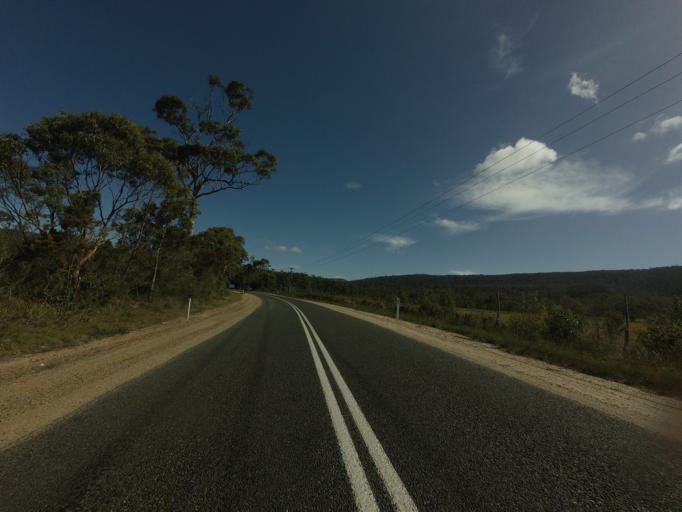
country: AU
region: Tasmania
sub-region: Break O'Day
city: St Helens
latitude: -41.8344
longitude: 148.2551
